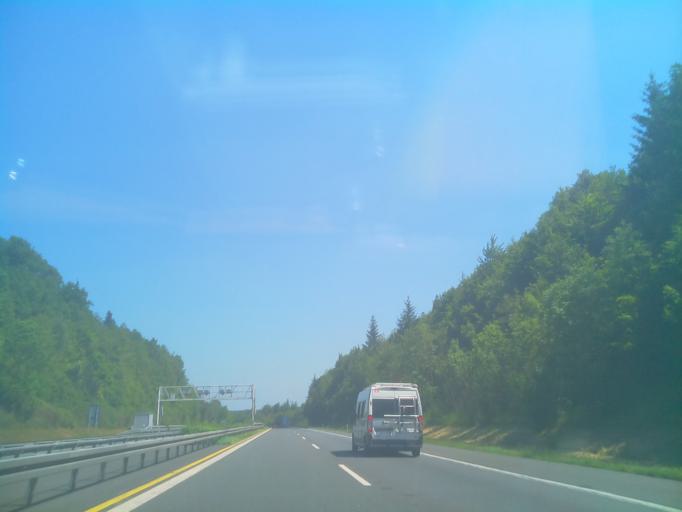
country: DE
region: Bavaria
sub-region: Regierungsbezirk Unterfranken
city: Kleinrinderfeld
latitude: 49.7121
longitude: 9.8117
